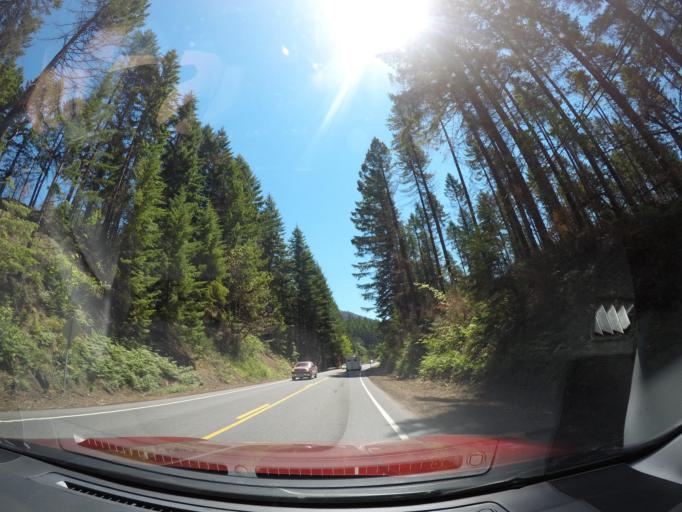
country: US
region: Oregon
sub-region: Linn County
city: Mill City
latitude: 44.7283
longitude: -122.1392
